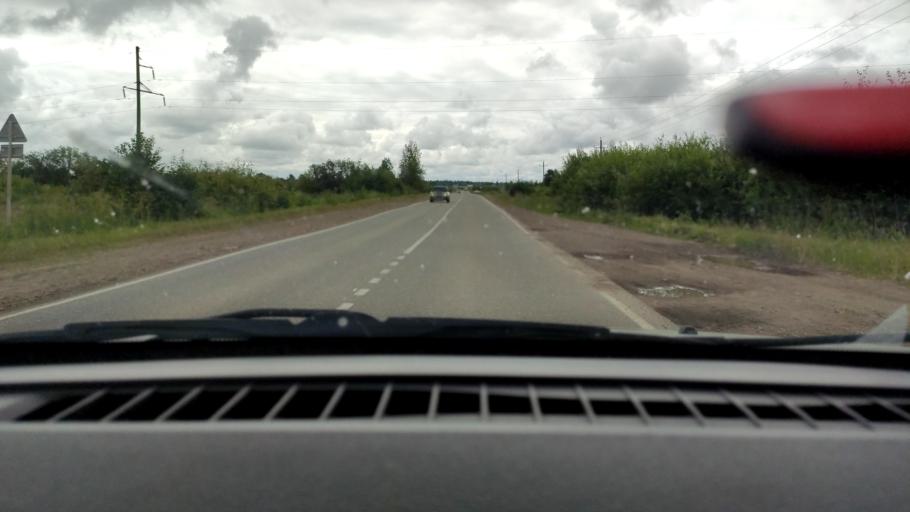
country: RU
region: Perm
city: Chaykovskaya
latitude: 58.0847
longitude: 55.6143
